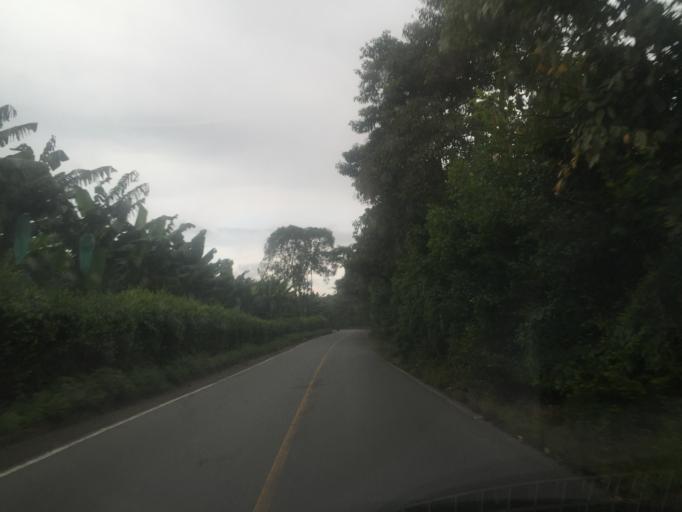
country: CO
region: Quindio
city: Armenia
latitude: 4.5146
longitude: -75.7301
